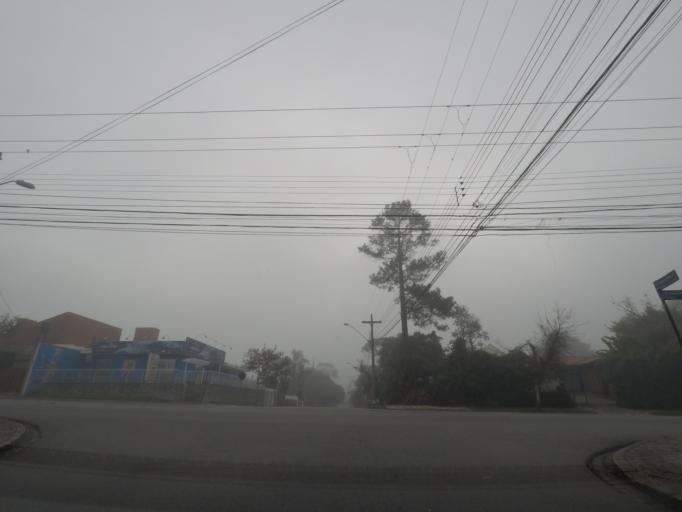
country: BR
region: Parana
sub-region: Curitiba
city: Curitiba
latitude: -25.4445
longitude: -49.2963
